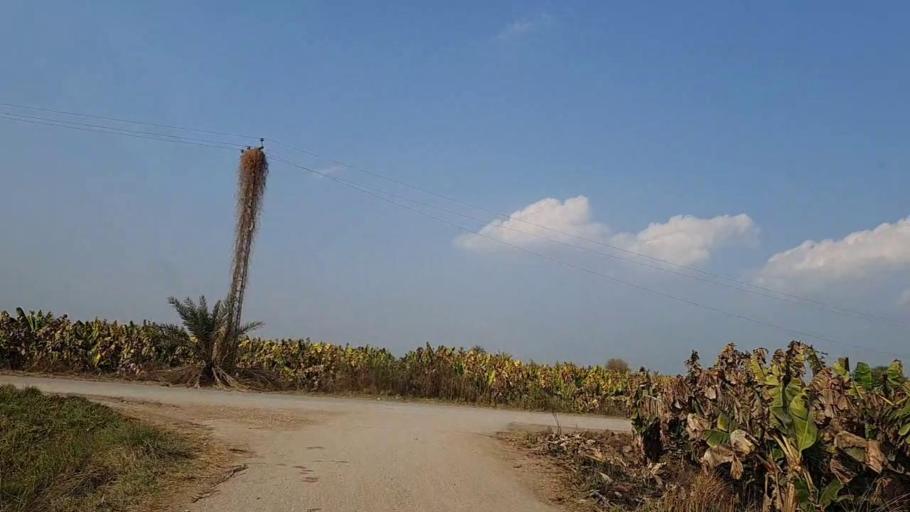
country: PK
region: Sindh
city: Nawabshah
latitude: 26.1523
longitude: 68.4005
